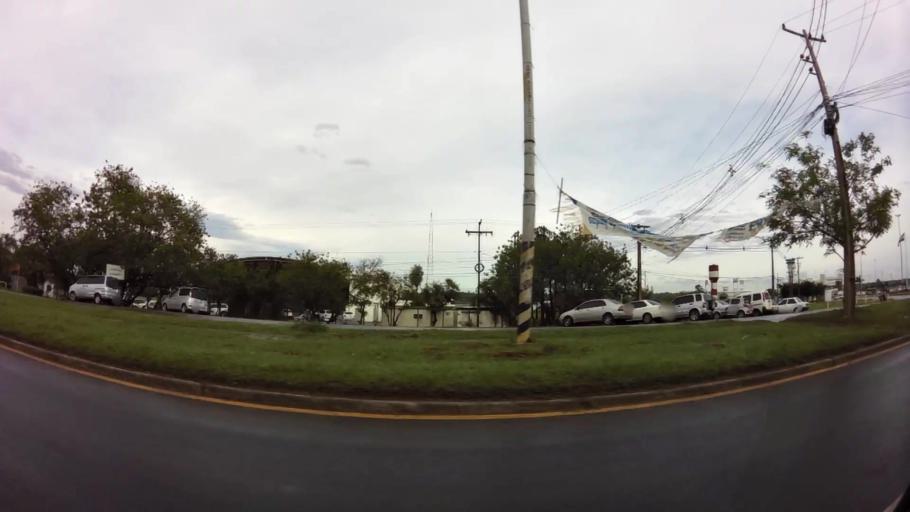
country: PY
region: Central
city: Limpio
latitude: -25.2457
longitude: -57.5115
